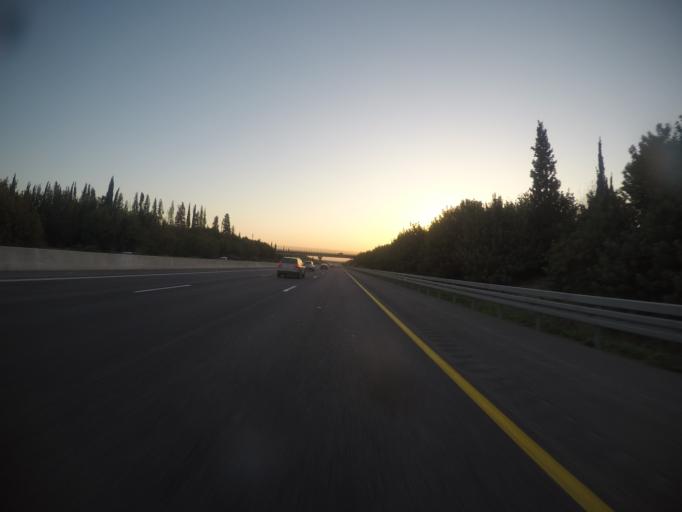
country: PS
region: West Bank
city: Nazlat `Isa
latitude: 32.4385
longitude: 35.0313
